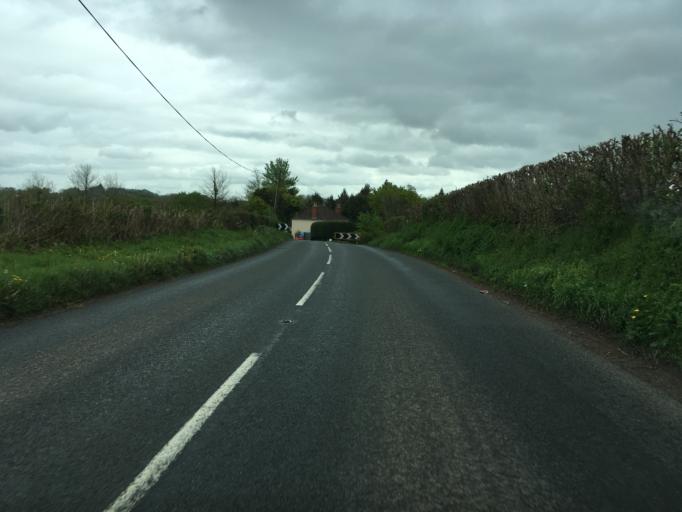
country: GB
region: England
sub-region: Bath and North East Somerset
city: Clutton
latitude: 51.3534
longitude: -2.5482
